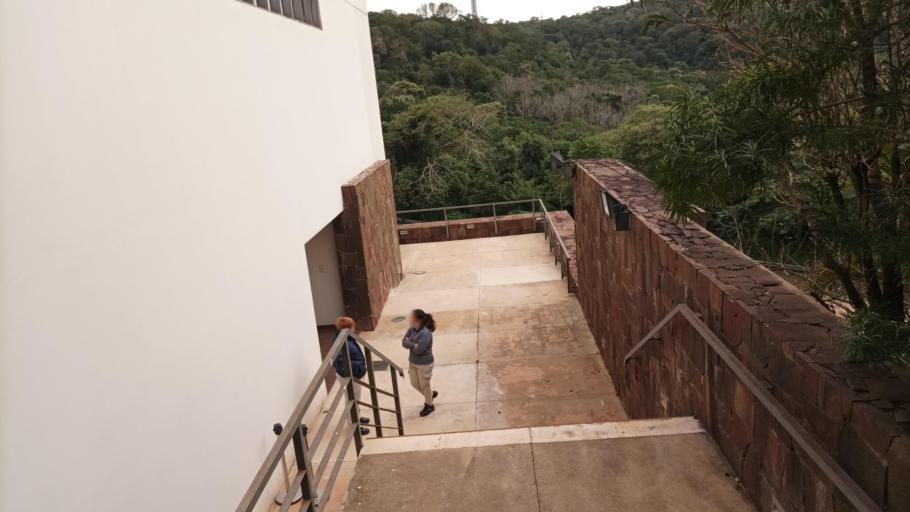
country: AR
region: Misiones
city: Cerro Cora
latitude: -27.4564
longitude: -55.5696
